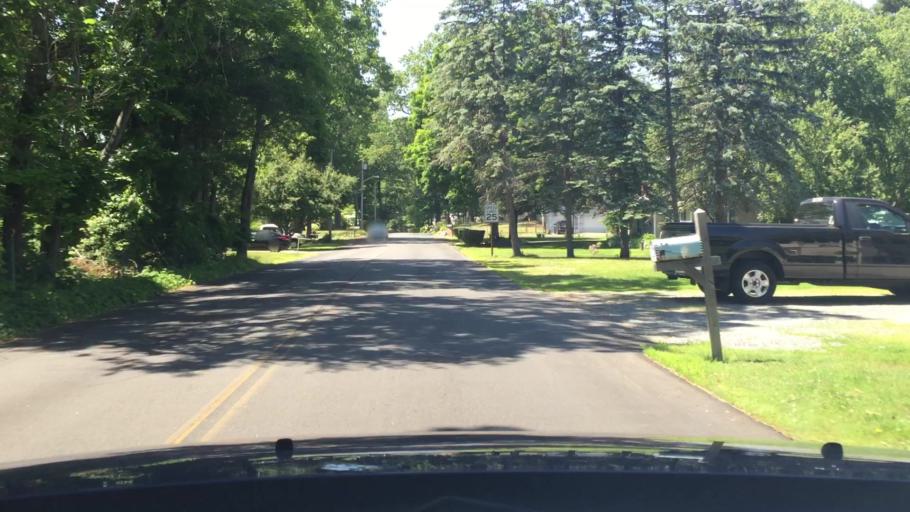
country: US
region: New Hampshire
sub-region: Rockingham County
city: Plaistow
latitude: 42.8188
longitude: -71.0966
